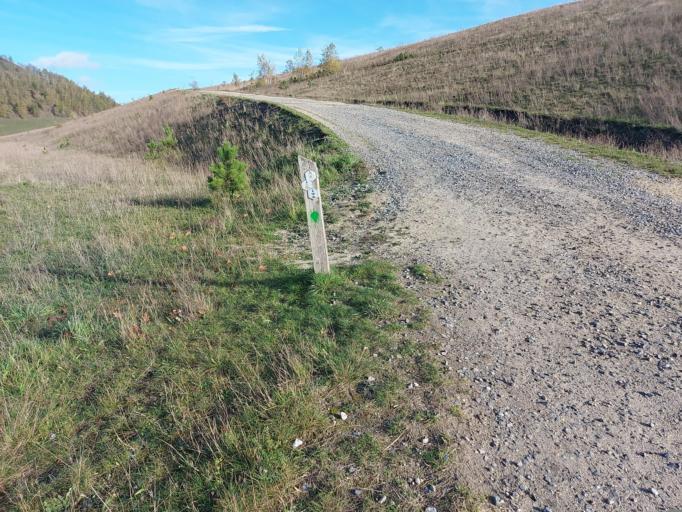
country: BE
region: Flanders
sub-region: Provincie Limburg
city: As
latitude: 51.0052
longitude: 5.5420
